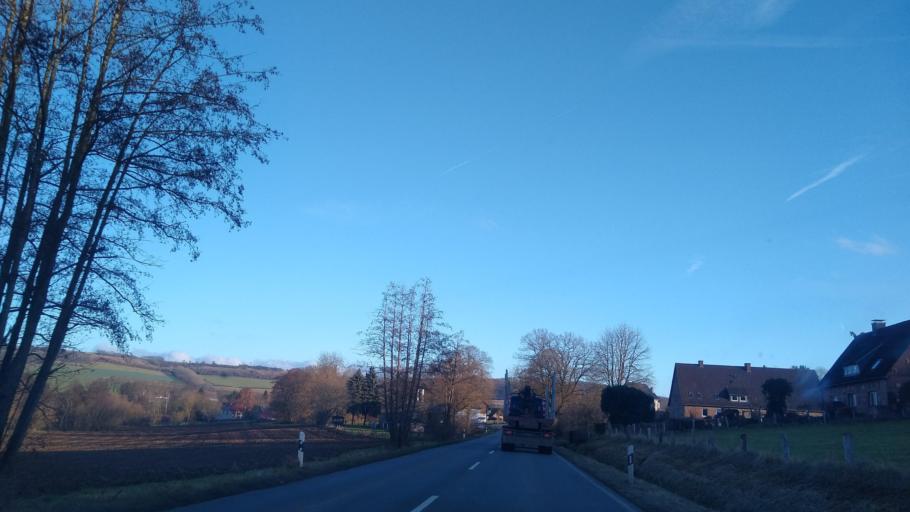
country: DE
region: North Rhine-Westphalia
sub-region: Regierungsbezirk Detmold
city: Hoexter
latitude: 51.8001
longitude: 9.3431
